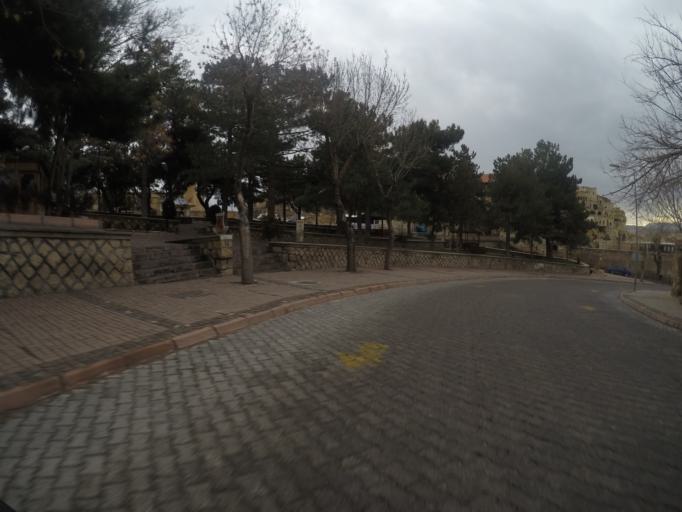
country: TR
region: Nevsehir
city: Urgub
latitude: 38.6325
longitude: 34.9092
